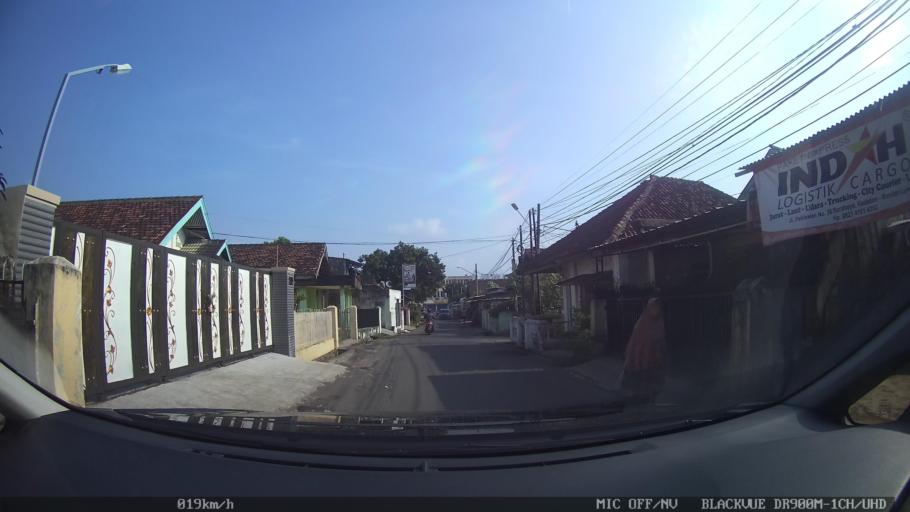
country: ID
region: Lampung
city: Kedaton
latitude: -5.3889
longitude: 105.2638
